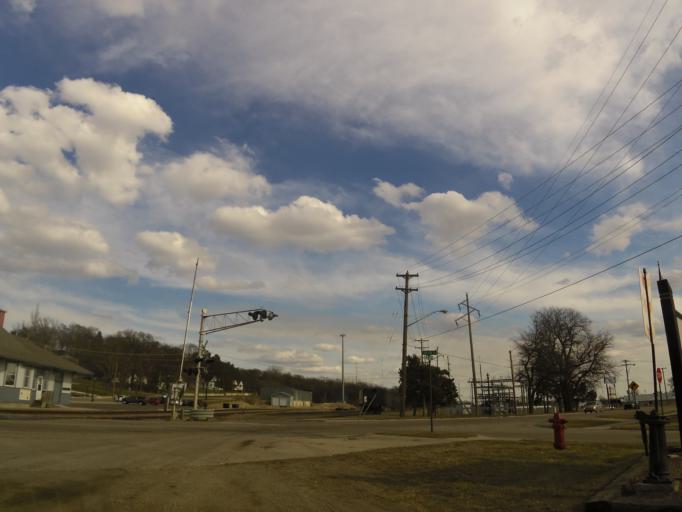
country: US
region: Minnesota
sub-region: Chippewa County
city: Montevideo
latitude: 44.9415
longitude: -95.7234
